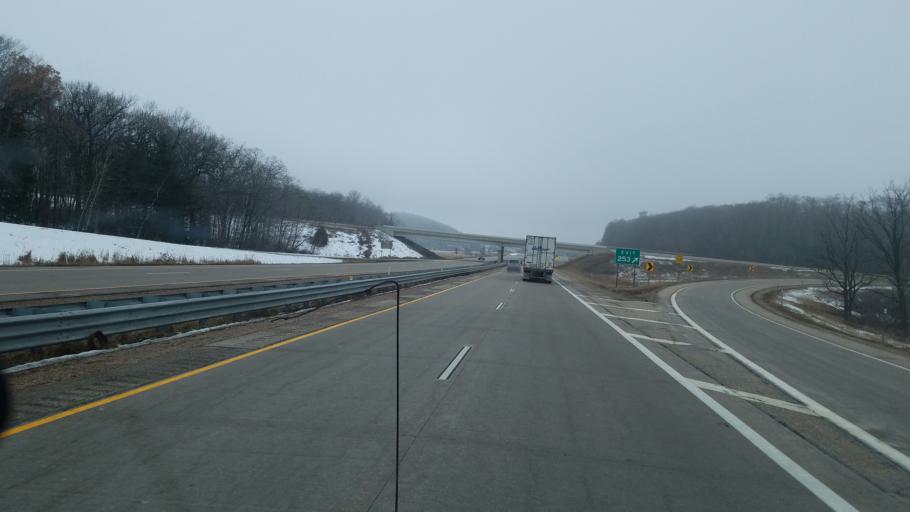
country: US
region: Wisconsin
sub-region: Waupaca County
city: Waupaca
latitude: 44.3376
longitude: -89.0671
